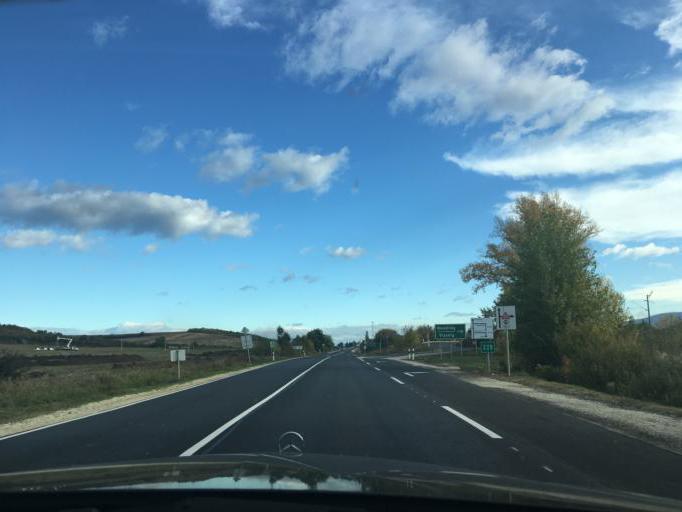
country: HU
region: Borsod-Abauj-Zemplen
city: Encs
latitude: 48.3882
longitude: 21.1557
